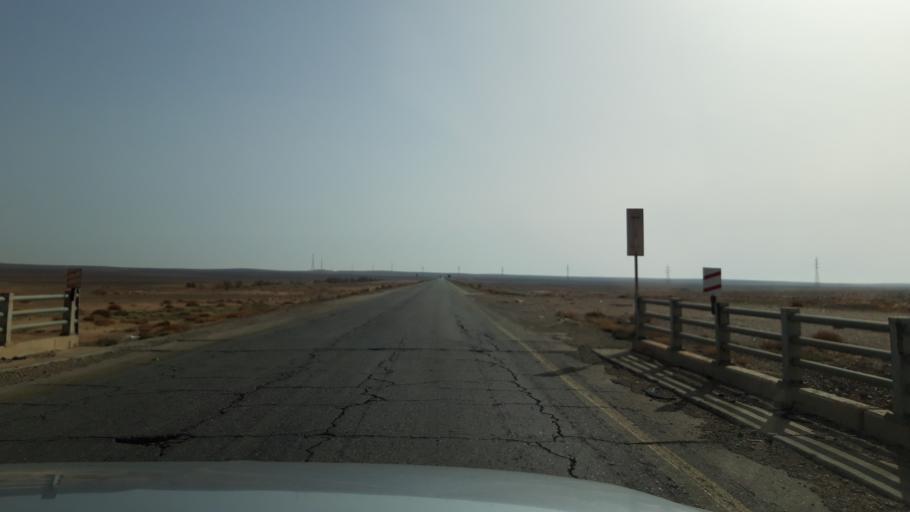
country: JO
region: Amman
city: Al Azraq ash Shamali
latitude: 31.7302
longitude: 36.4915
